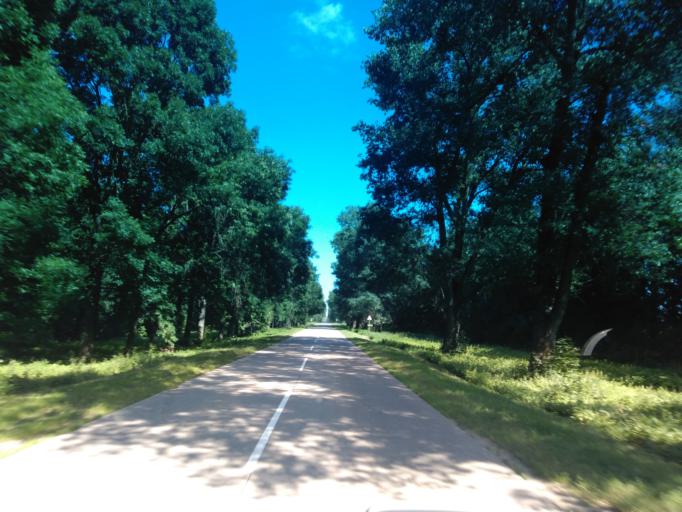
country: BY
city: Fanipol
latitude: 53.6671
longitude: 27.3373
